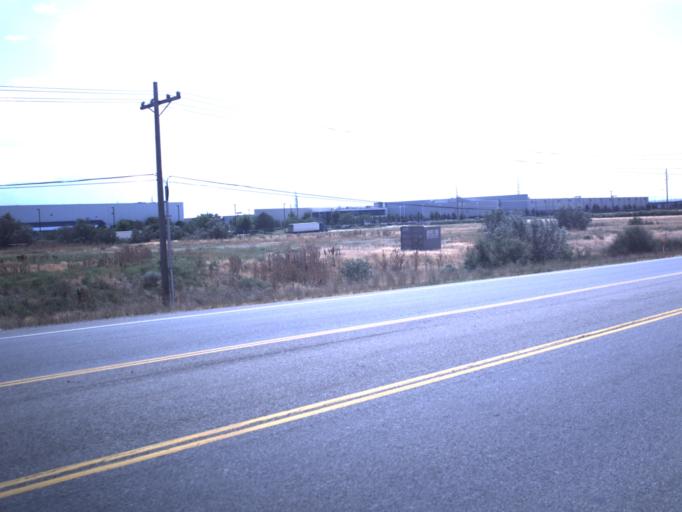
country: US
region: Utah
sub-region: Salt Lake County
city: West Valley City
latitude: 40.7654
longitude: -112.0251
